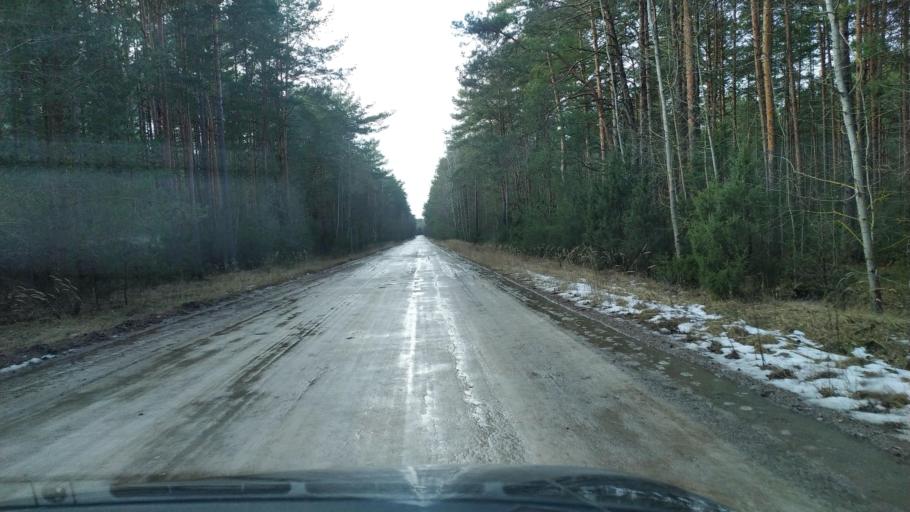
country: BY
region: Brest
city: Kamyanyets
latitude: 52.4269
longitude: 23.9861
